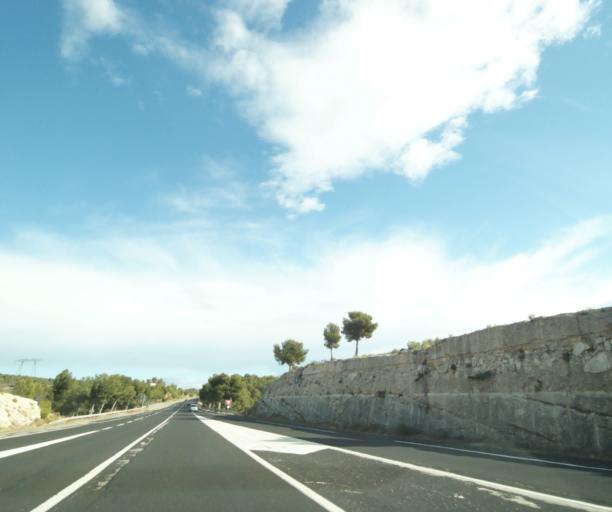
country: FR
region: Provence-Alpes-Cote d'Azur
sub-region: Departement des Bouches-du-Rhone
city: Sausset-les-Pins
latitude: 43.3459
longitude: 5.0621
